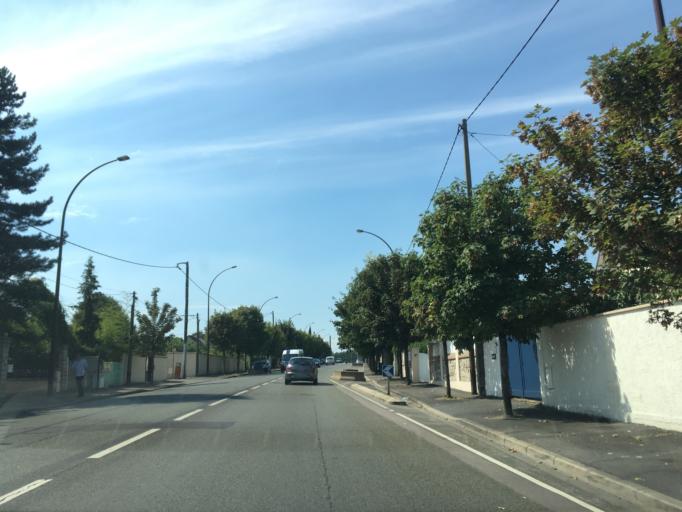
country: FR
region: Ile-de-France
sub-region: Departement des Yvelines
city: Gargenville
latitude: 48.9751
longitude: 1.8054
